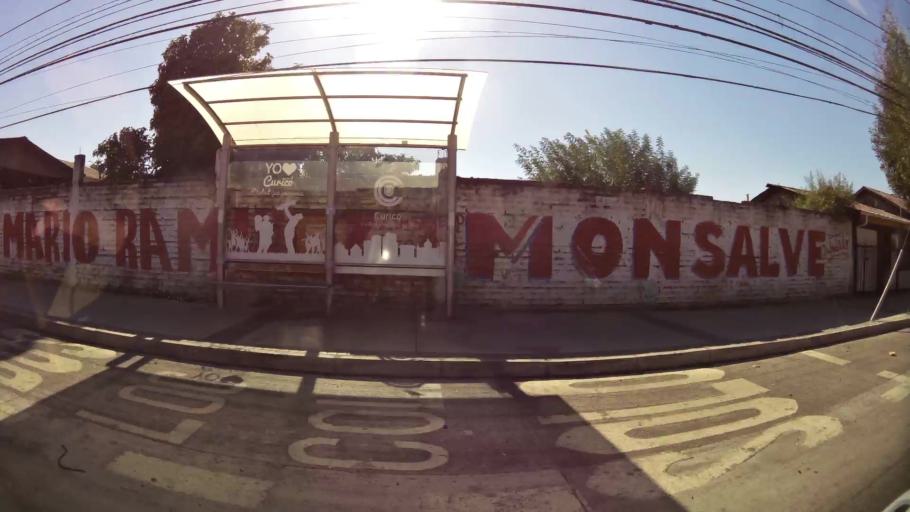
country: CL
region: Maule
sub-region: Provincia de Curico
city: Curico
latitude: -34.9882
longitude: -71.2488
